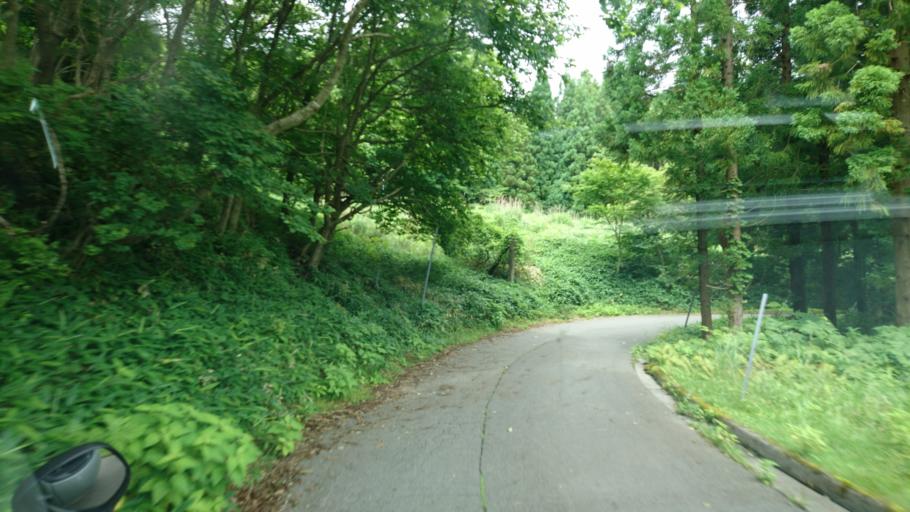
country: JP
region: Iwate
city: Ofunato
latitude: 39.1360
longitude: 141.7597
